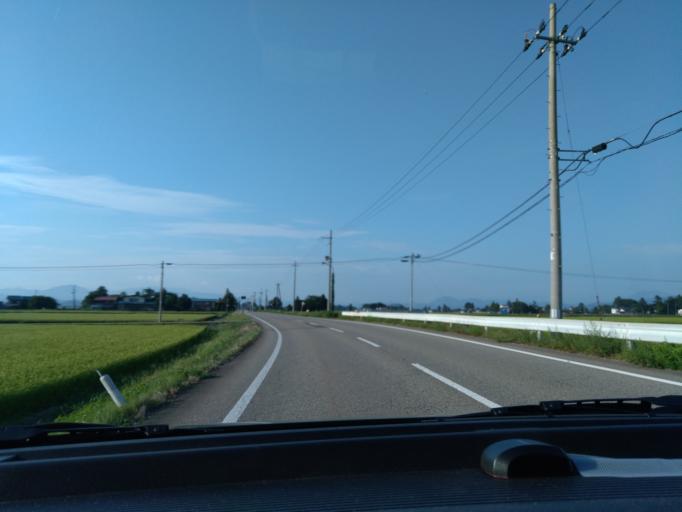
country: JP
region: Akita
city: Kakunodatemachi
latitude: 39.5176
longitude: 140.5586
